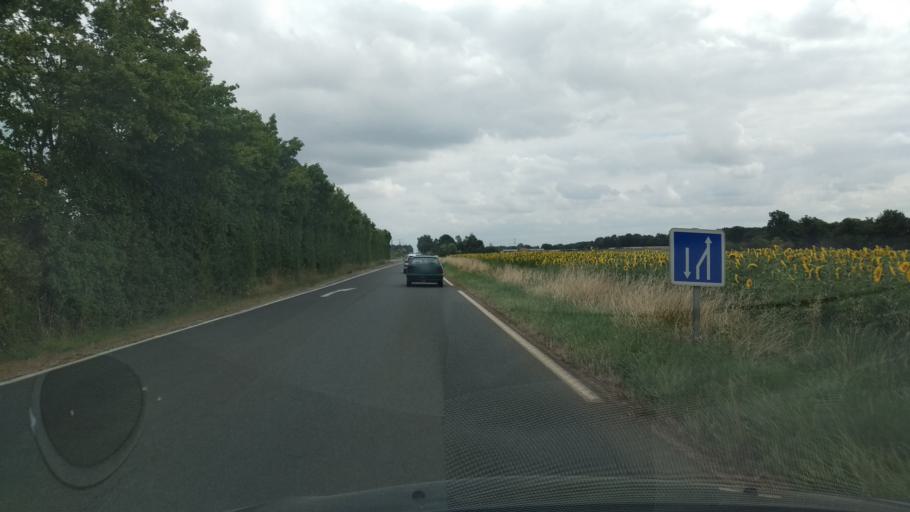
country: FR
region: Poitou-Charentes
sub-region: Departement de la Vienne
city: La Villedieu-du-Clain
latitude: 46.4158
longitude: 0.3852
